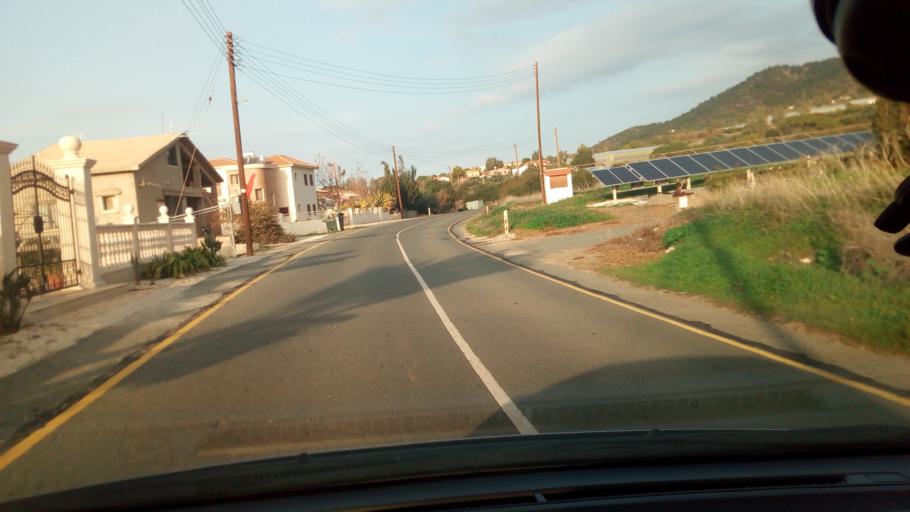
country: CY
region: Pafos
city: Polis
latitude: 35.1315
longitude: 32.5185
